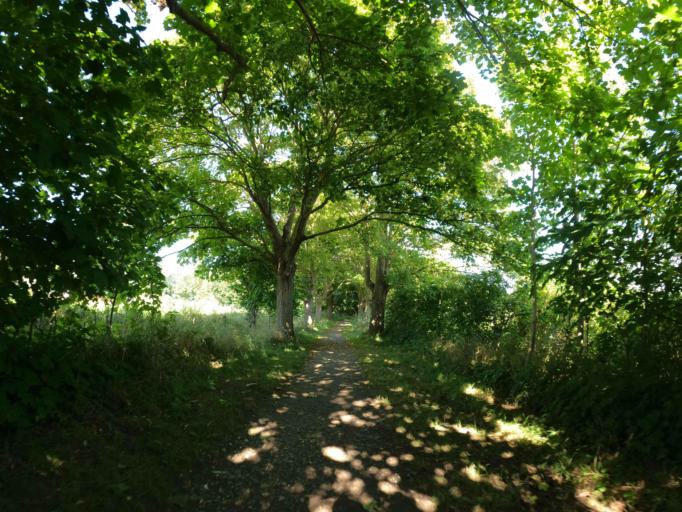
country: DE
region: Mecklenburg-Vorpommern
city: Prohn
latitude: 54.4090
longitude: 13.0176
